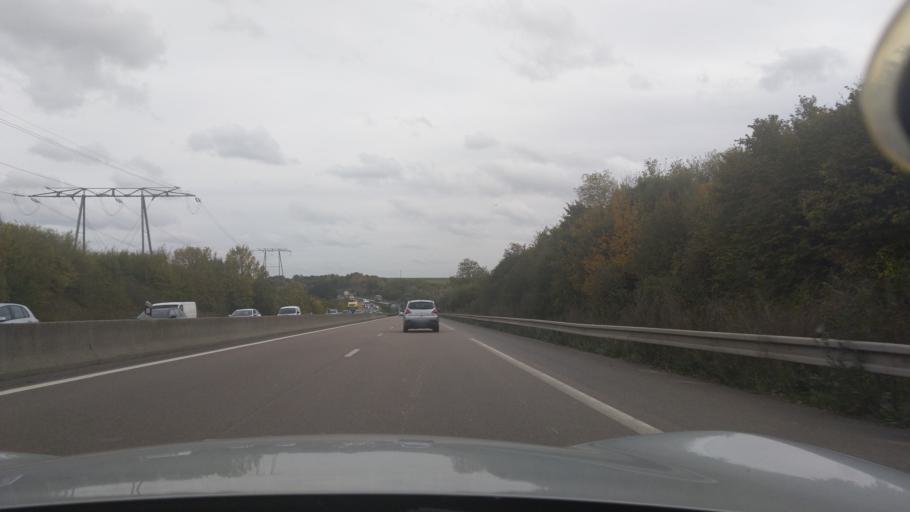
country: FR
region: Ile-de-France
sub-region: Departement du Val-d'Oise
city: Louvres
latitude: 49.0374
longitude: 2.4852
